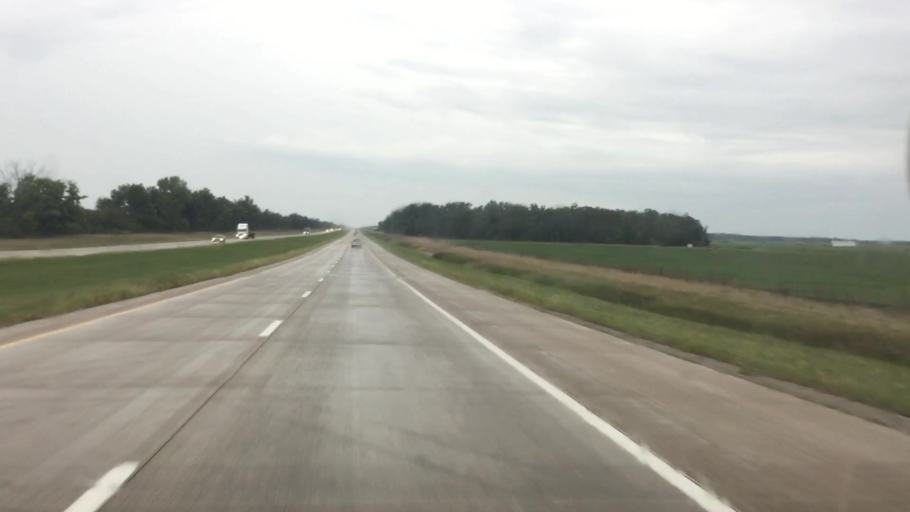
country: US
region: Ohio
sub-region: Defiance County
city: Defiance
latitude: 41.2669
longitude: -84.4320
